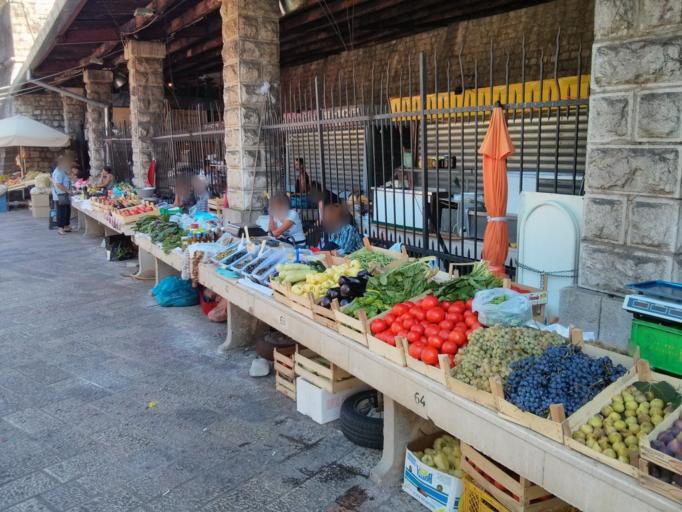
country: ME
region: Kotor
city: Kotor
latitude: 42.4242
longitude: 18.7700
